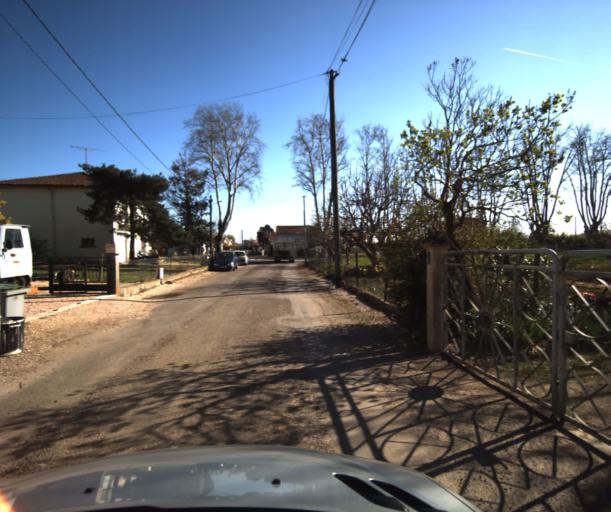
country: FR
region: Midi-Pyrenees
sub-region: Departement du Tarn-et-Garonne
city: Bressols
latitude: 43.9676
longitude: 1.3352
